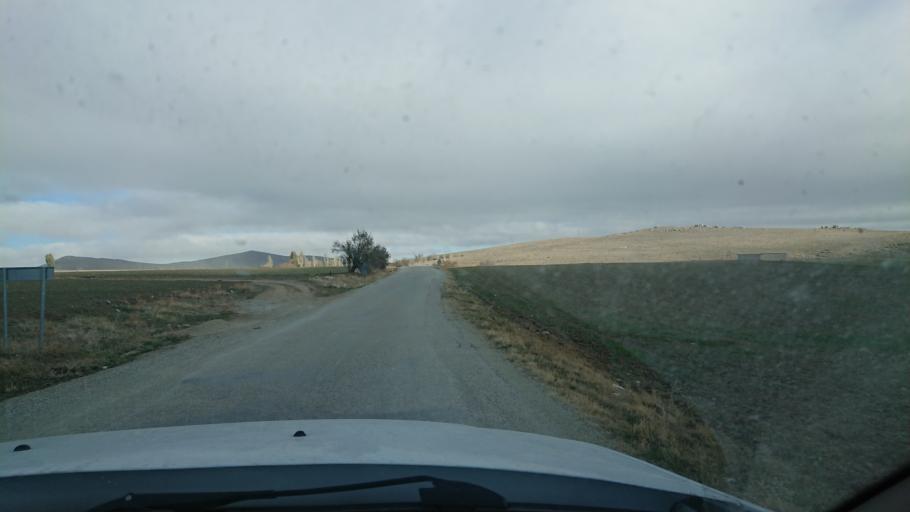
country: TR
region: Aksaray
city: Ortakoy
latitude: 38.7635
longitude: 34.0129
